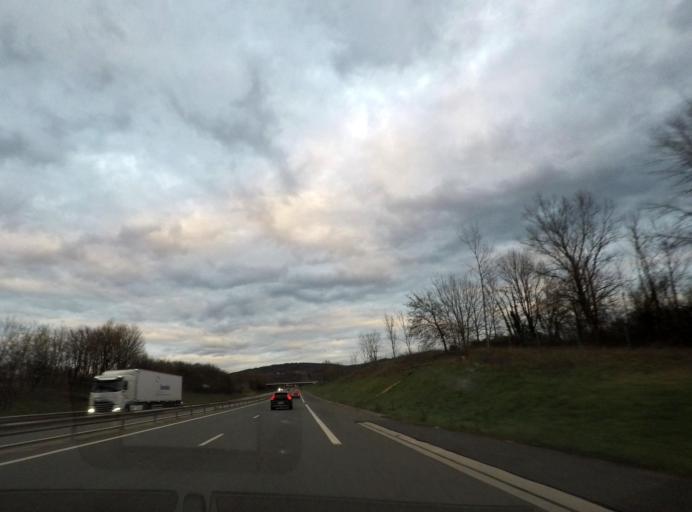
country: FR
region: Rhone-Alpes
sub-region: Departement de l'Ain
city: Poncin
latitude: 46.0936
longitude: 5.4088
